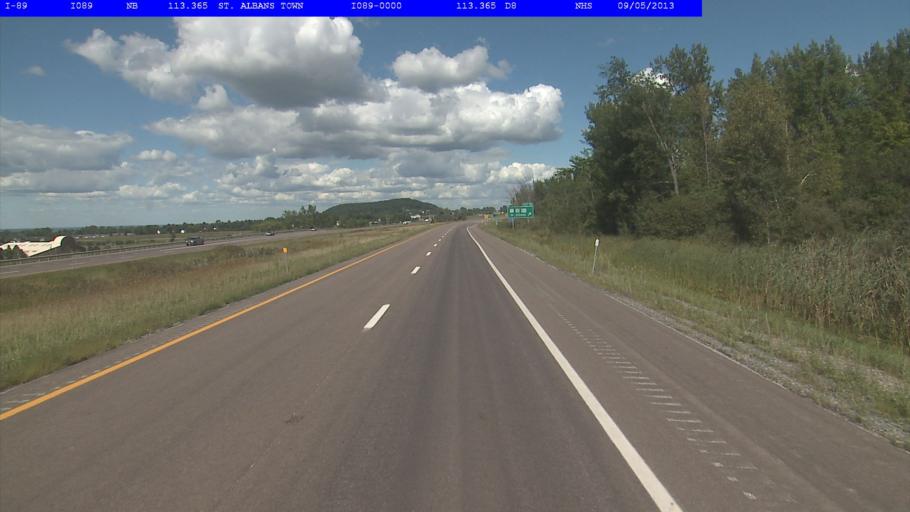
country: US
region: Vermont
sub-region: Franklin County
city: Saint Albans
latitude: 44.7895
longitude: -73.0714
